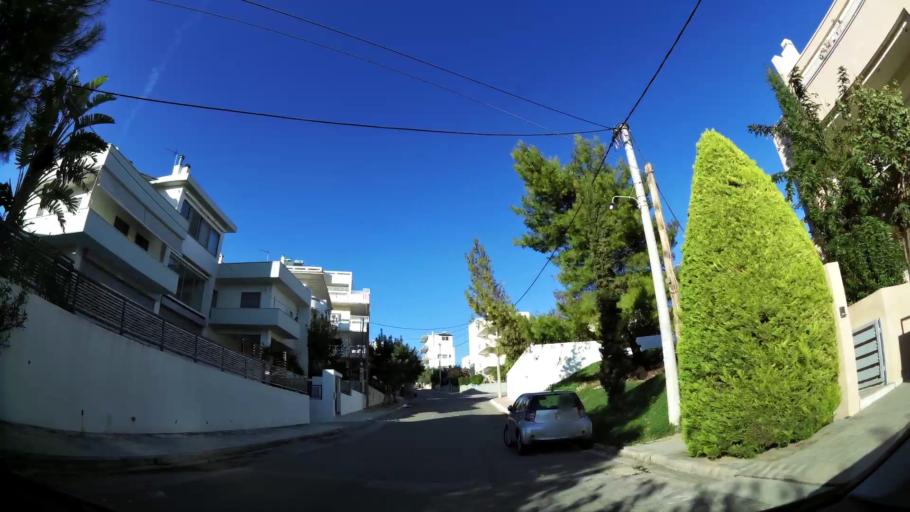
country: GR
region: Attica
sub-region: Nomarchia Anatolikis Attikis
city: Rafina
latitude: 38.0220
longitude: 24.0001
